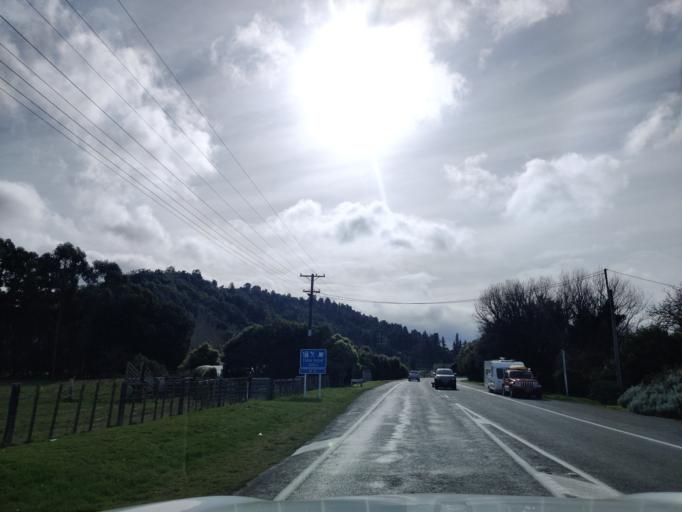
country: NZ
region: Manawatu-Wanganui
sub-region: Ruapehu District
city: Waiouru
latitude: -39.8118
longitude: 175.7854
